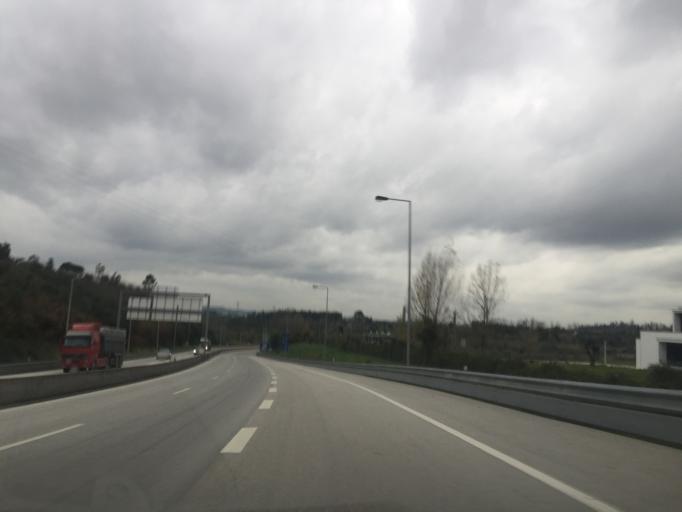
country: PT
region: Coimbra
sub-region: Condeixa-A-Nova
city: Condeixa-a-Nova
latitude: 40.1296
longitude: -8.4869
